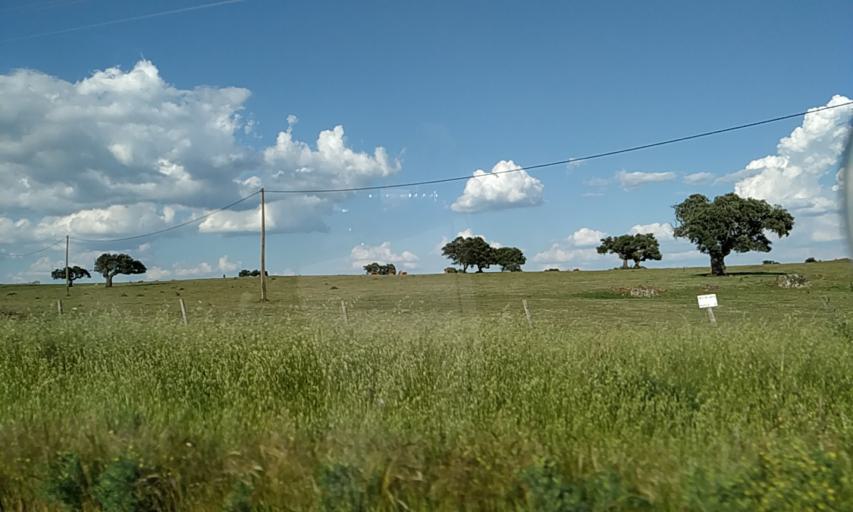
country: PT
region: Portalegre
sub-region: Portalegre
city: Urra
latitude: 39.1313
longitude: -7.4481
